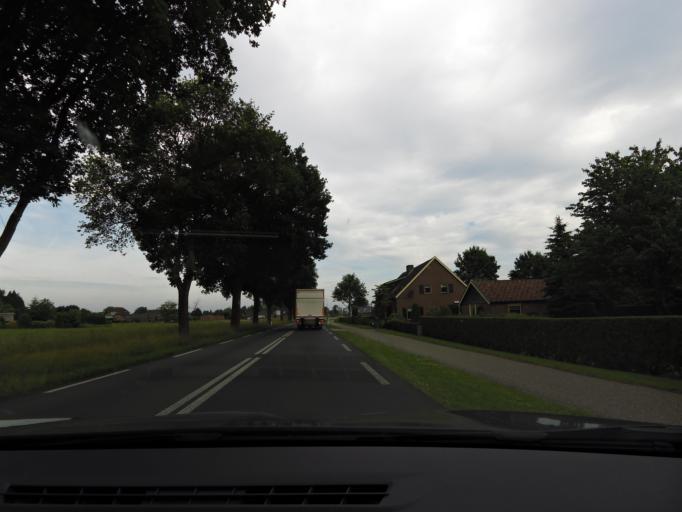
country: NL
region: Gelderland
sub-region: Gemeente Apeldoorn
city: Loenen
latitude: 52.1064
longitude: 6.0371
